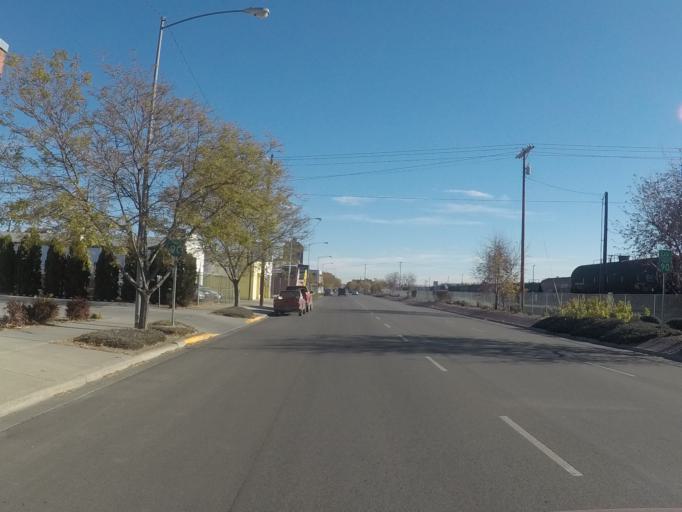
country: US
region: Montana
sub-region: Yellowstone County
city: Billings
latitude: 45.7772
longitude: -108.5134
